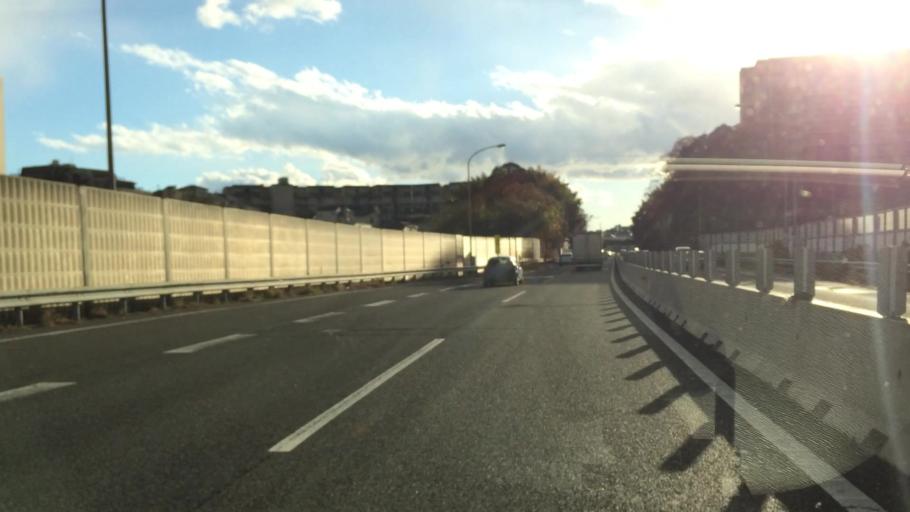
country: JP
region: Kanagawa
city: Fujisawa
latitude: 35.4166
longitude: 139.5369
